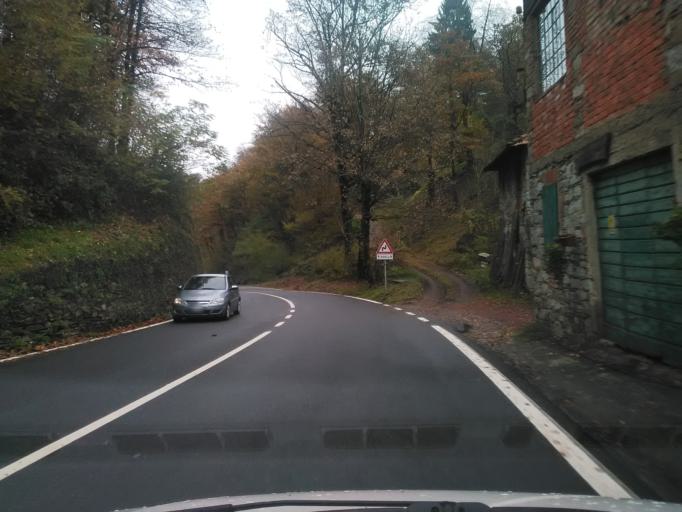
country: IT
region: Piedmont
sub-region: Provincia di Novara
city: Pogno
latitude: 45.7424
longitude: 8.3616
